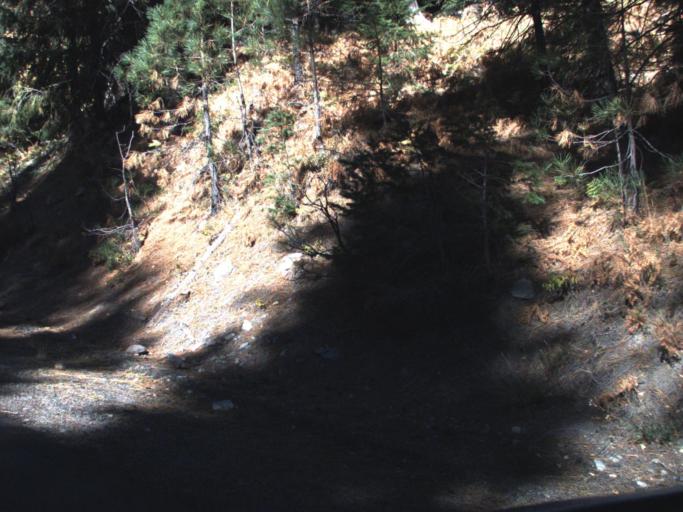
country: US
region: Washington
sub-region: Yakima County
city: Tieton
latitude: 46.6518
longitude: -121.2934
